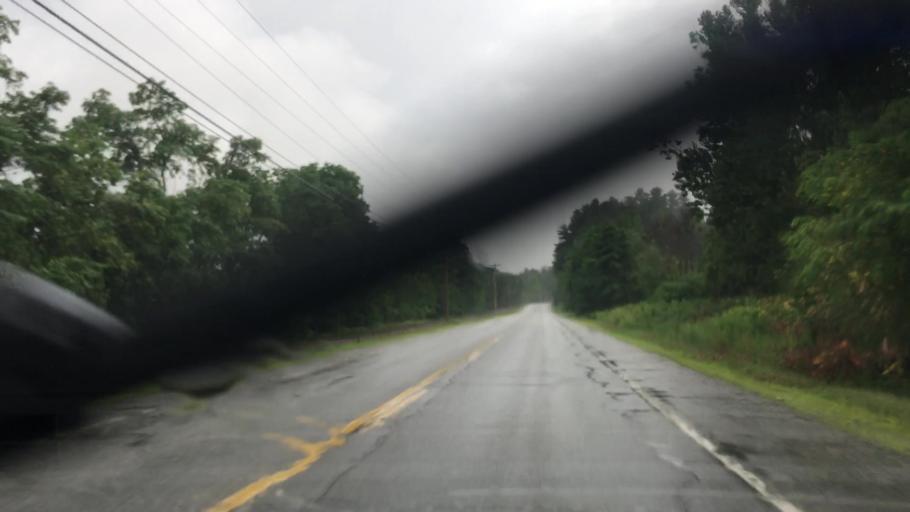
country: US
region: Maine
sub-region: Kennebec County
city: Pittston
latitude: 44.2129
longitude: -69.7630
